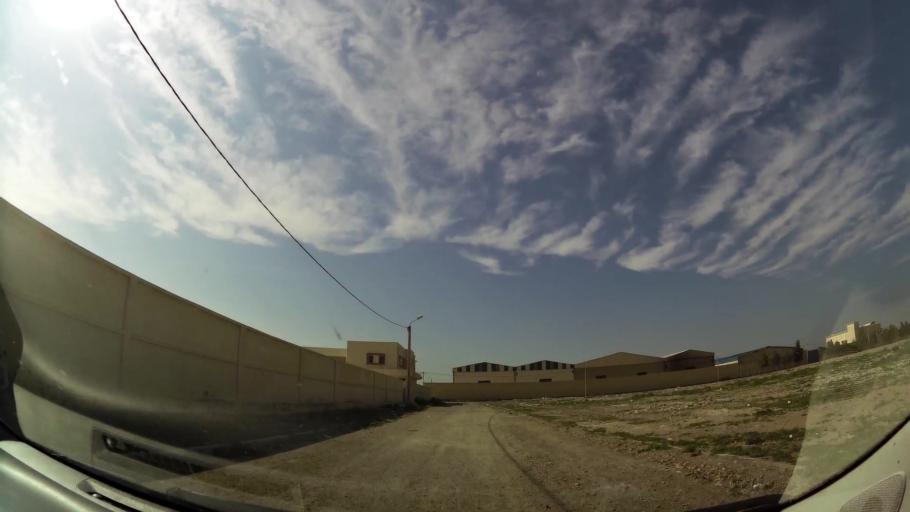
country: MA
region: Oriental
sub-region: Oujda-Angad
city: Oujda
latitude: 34.6995
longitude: -1.8818
